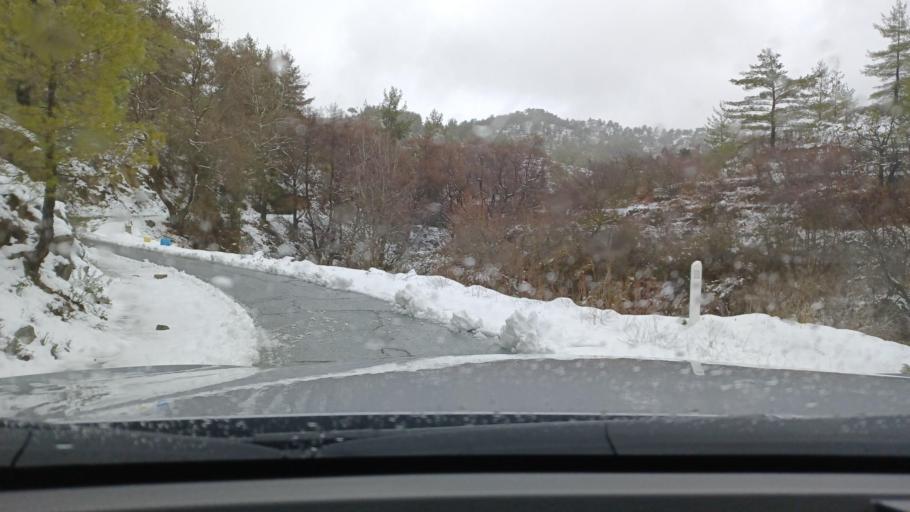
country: CY
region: Limassol
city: Pelendri
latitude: 34.9140
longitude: 32.9506
